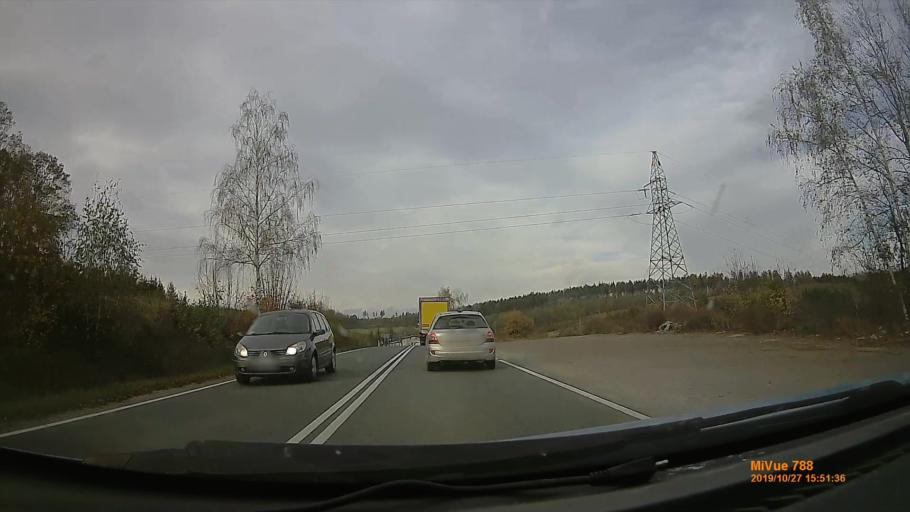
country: PL
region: Lower Silesian Voivodeship
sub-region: Powiat klodzki
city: Bozkow
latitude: 50.5277
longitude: 16.5827
